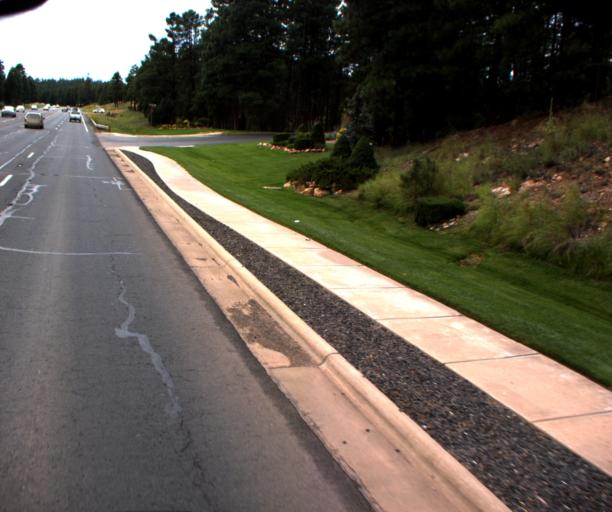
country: US
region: Arizona
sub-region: Navajo County
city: Show Low
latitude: 34.2293
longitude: -110.0276
